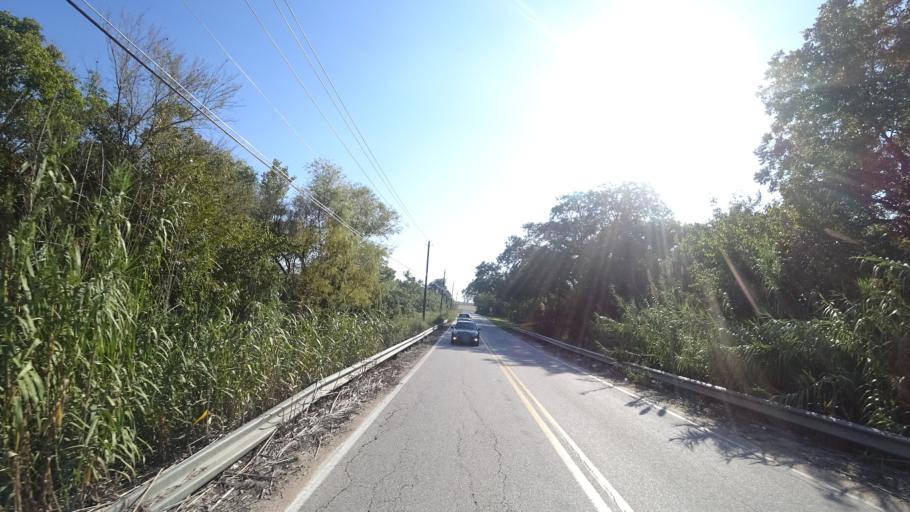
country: US
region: Texas
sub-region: Travis County
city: Wells Branch
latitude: 30.3440
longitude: -97.6617
